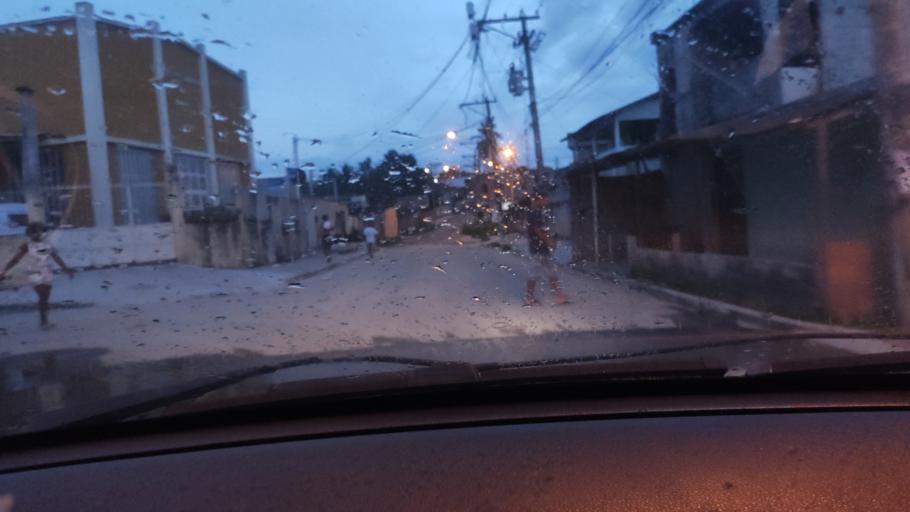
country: BR
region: Rio de Janeiro
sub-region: Itaborai
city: Itaborai
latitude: -22.7780
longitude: -42.9403
